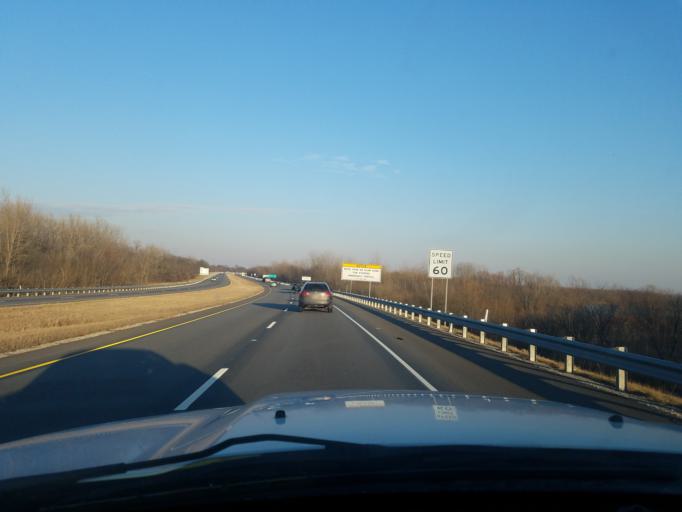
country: US
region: Indiana
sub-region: Vanderburgh County
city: Evansville
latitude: 37.9359
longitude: -87.5276
